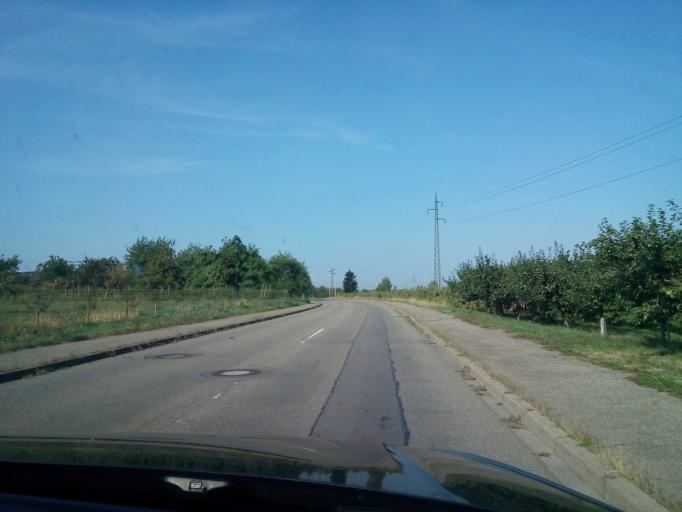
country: DE
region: Baden-Wuerttemberg
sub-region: Freiburg Region
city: Oberkirch
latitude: 48.5413
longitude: 8.0682
